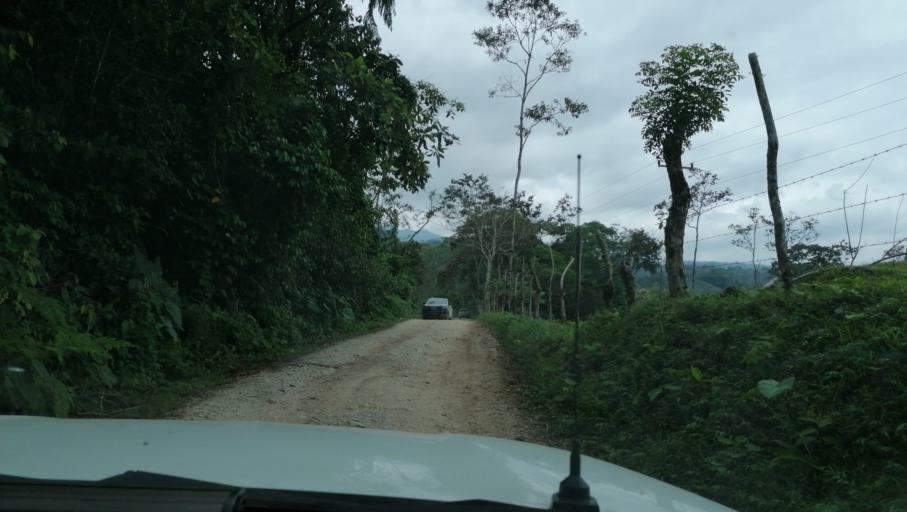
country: MX
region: Chiapas
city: Ocotepec
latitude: 17.2803
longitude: -93.2275
